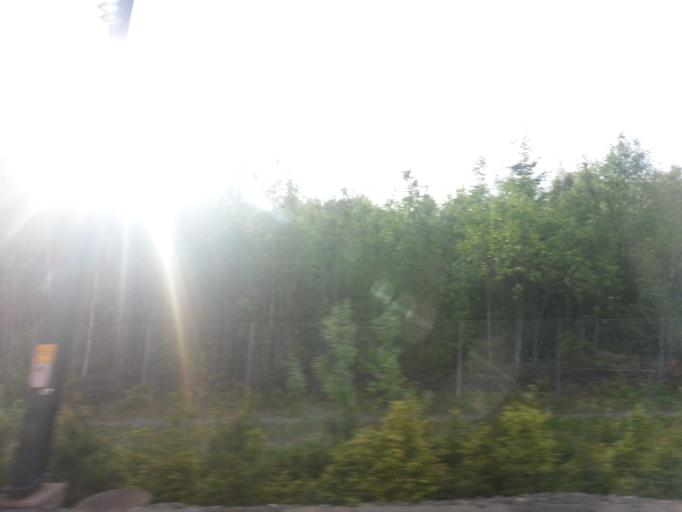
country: NO
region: Akershus
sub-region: Ullensaker
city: Klofta
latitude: 60.0899
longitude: 11.1407
